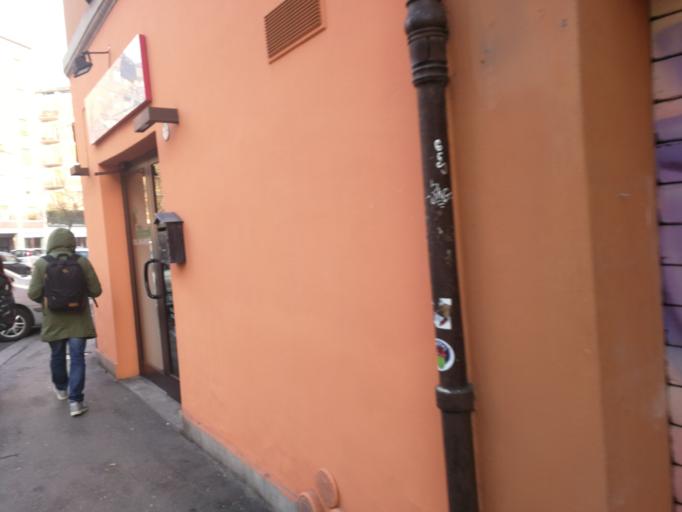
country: IT
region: Emilia-Romagna
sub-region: Provincia di Bologna
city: Bologna
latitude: 44.4985
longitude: 11.3321
